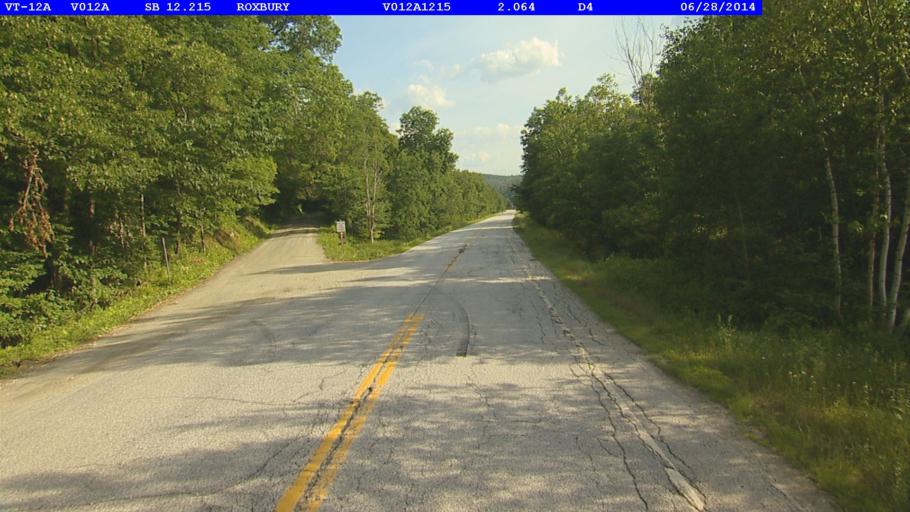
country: US
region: Vermont
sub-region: Washington County
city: Northfield
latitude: 44.0583
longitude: -72.7427
